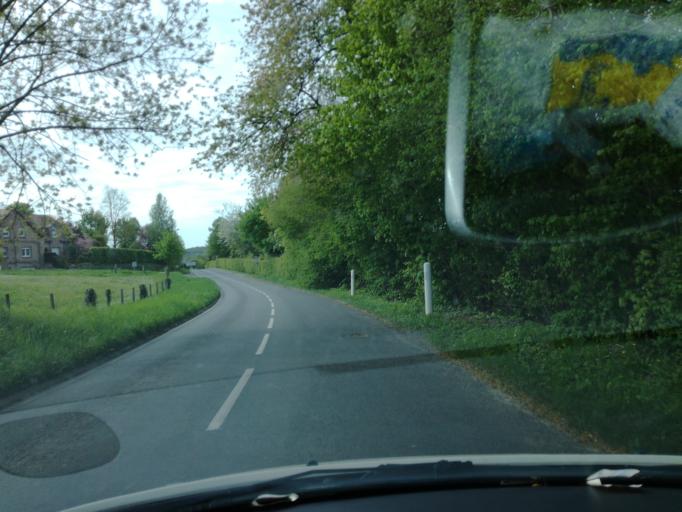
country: FR
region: Picardie
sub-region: Departement de la Somme
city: Poix-de-Picardie
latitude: 49.7810
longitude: 1.9882
